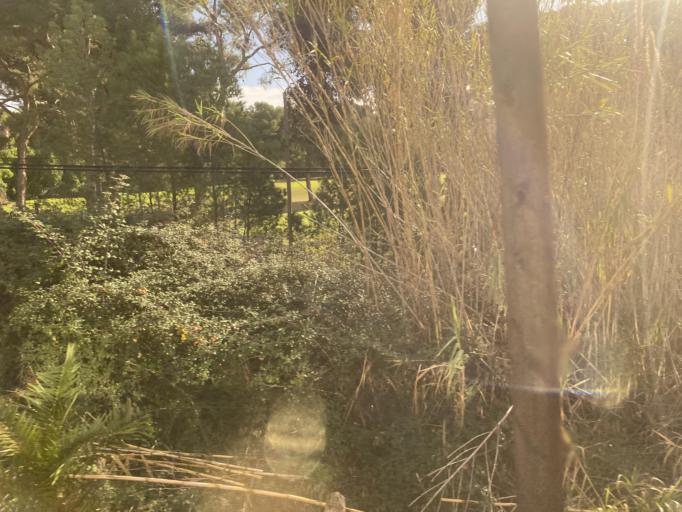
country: ES
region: Catalonia
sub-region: Provincia de Barcelona
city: Sitges
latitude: 41.2293
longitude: 1.7833
